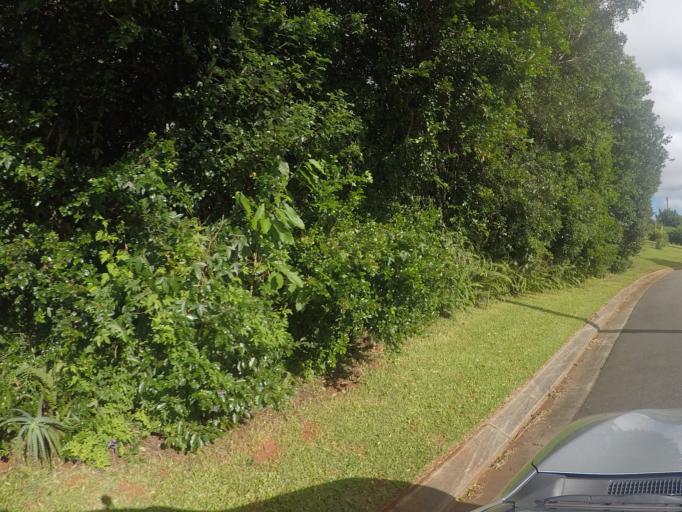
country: AU
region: Queensland
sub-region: Sunshine Coast
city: Nambour
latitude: -26.6198
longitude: 152.8659
